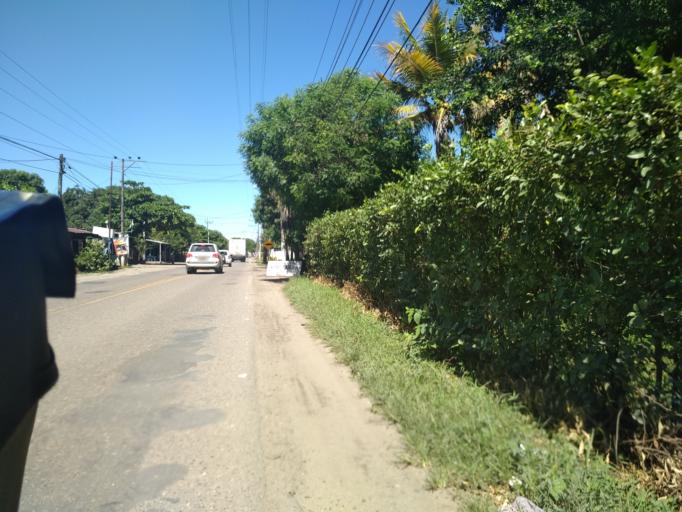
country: CO
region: Cundinamarca
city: Puerto Salgar
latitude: 5.4720
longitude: -74.6488
